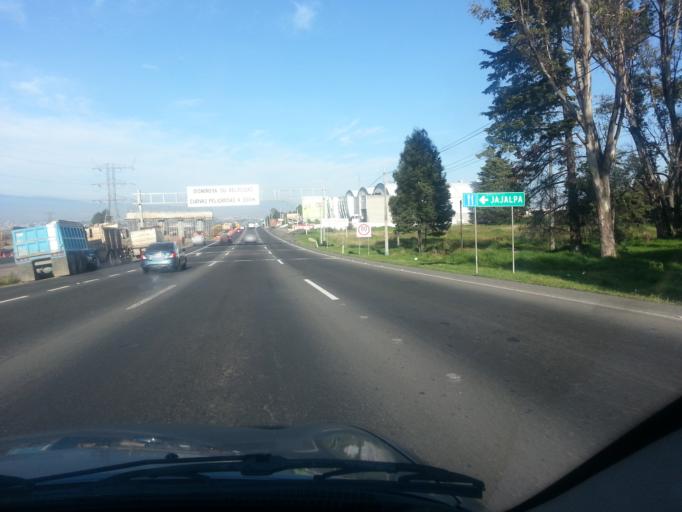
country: MX
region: Mexico
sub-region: Lerma
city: Fraccionamiento y Club de Golf los Encinos
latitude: 19.2826
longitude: -99.4778
